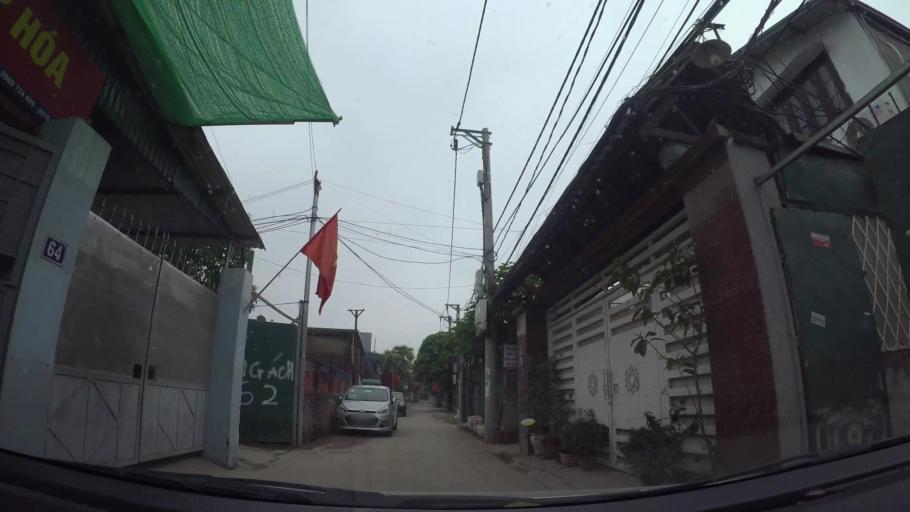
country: VN
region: Ha Noi
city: Tay Ho
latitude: 21.0719
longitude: 105.8284
